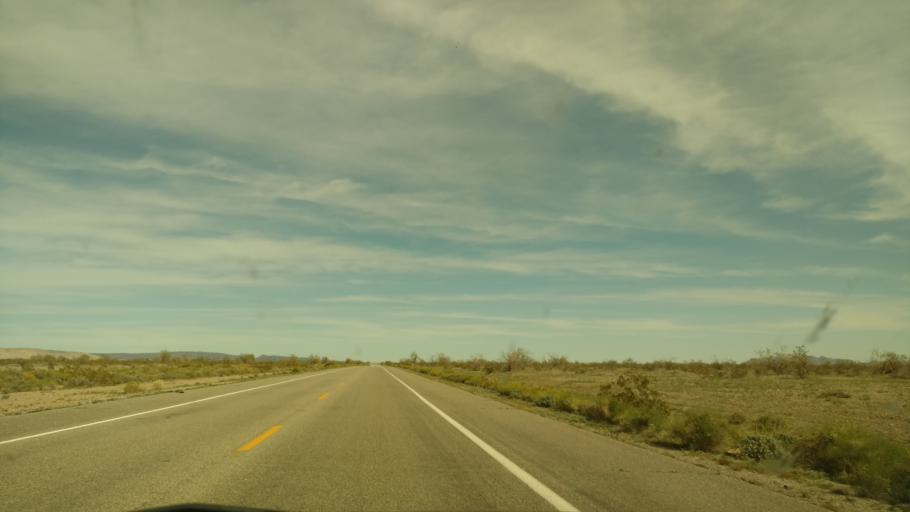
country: MX
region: Baja California
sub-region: Mexicali
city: Ejido Netzahualcoyotl
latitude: 33.0150
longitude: -115.0327
